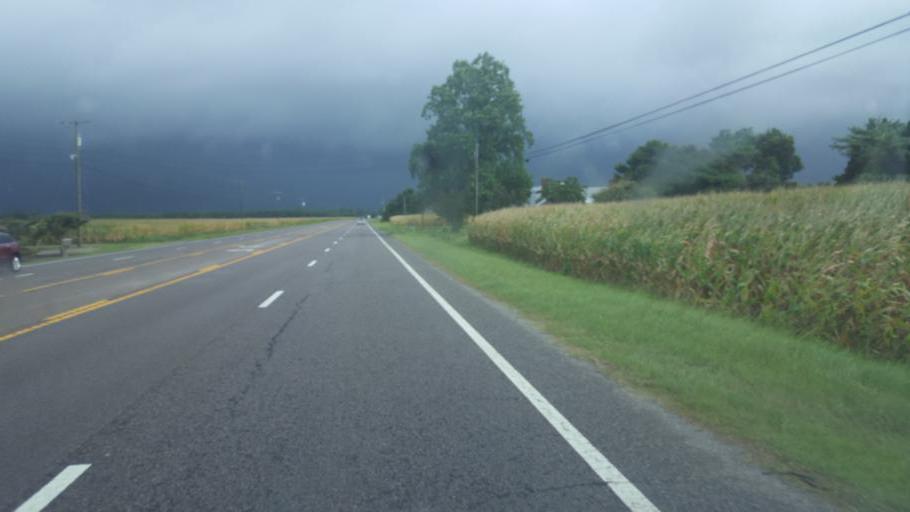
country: US
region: North Carolina
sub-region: Dare County
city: Southern Shores
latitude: 36.1881
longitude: -75.8639
